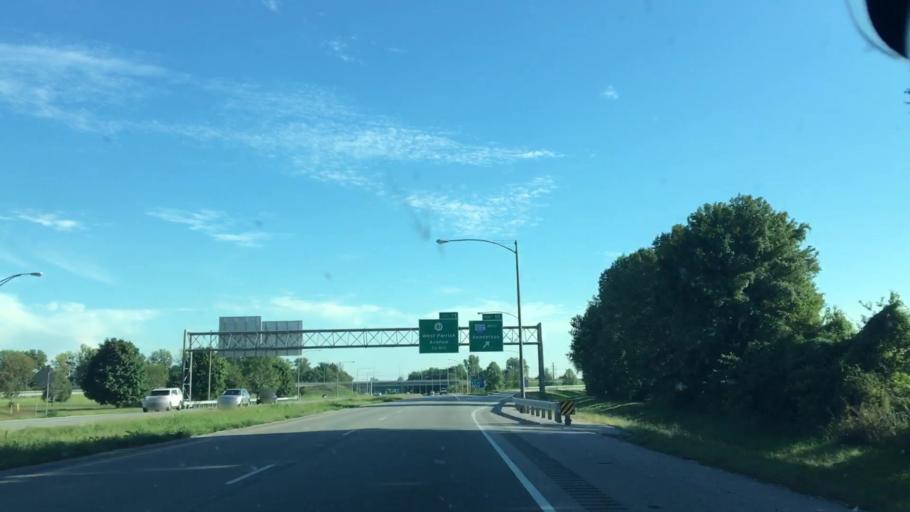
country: US
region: Kentucky
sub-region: Daviess County
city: Owensboro
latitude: 37.7702
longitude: -87.1651
